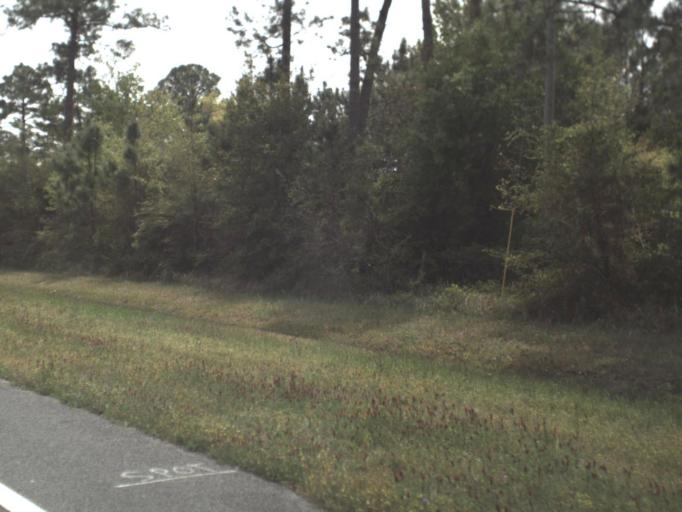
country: US
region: Florida
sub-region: Escambia County
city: Myrtle Grove
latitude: 30.3552
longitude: -87.3562
